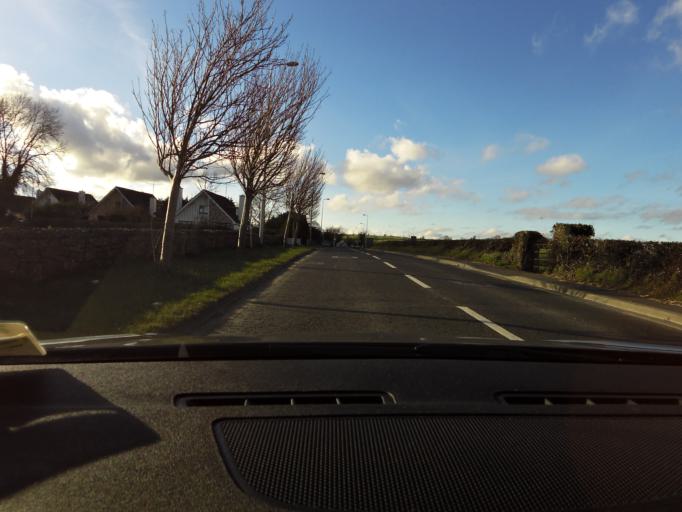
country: IE
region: Connaught
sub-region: Roscommon
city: Roscommon
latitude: 53.6410
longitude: -8.1932
